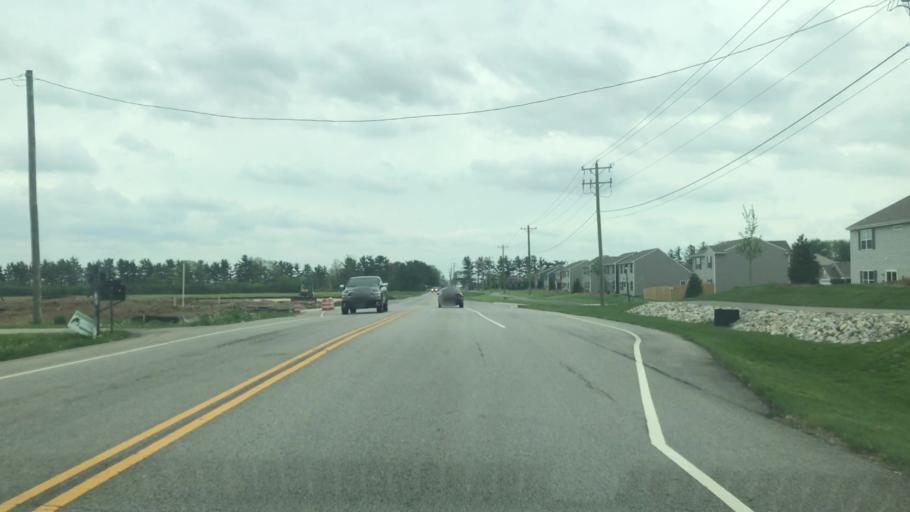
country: US
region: Indiana
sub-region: Johnson County
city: New Whiteland
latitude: 39.5831
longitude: -86.0830
